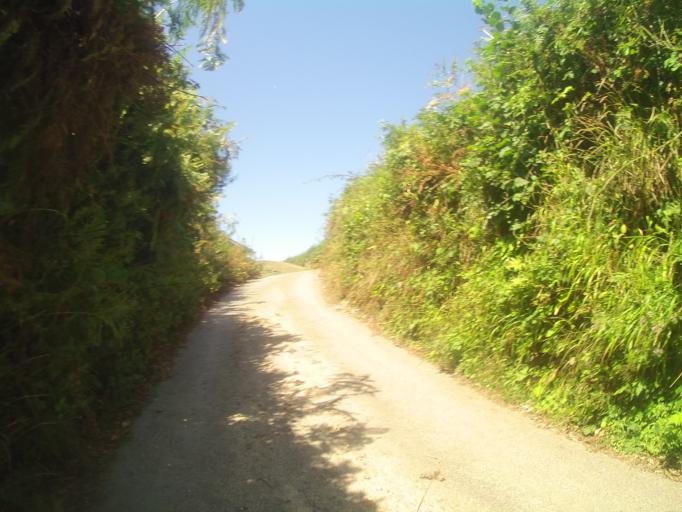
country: GB
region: England
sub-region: Devon
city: Dartmouth
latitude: 50.3638
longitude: -3.6233
